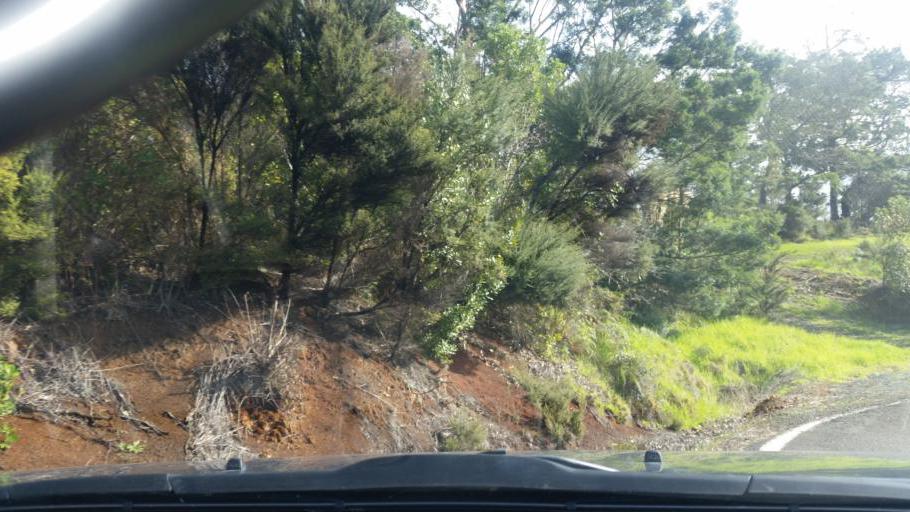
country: NZ
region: Auckland
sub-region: Auckland
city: Wellsford
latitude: -36.2564
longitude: 174.2495
